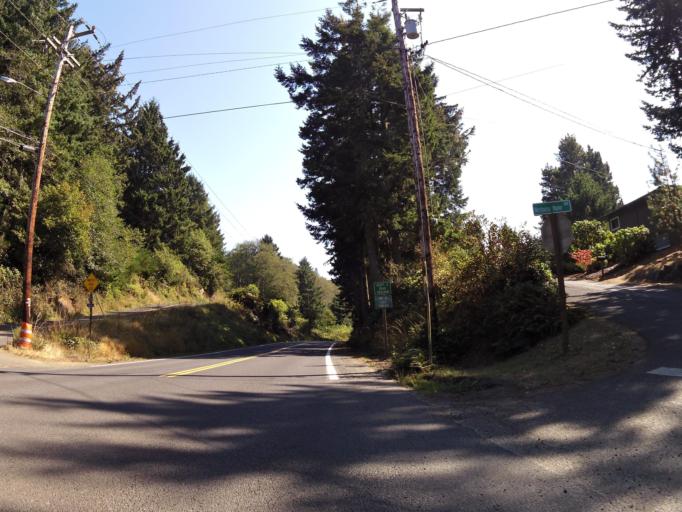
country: US
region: Oregon
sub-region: Tillamook County
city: Pacific City
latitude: 45.1958
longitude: -123.9567
